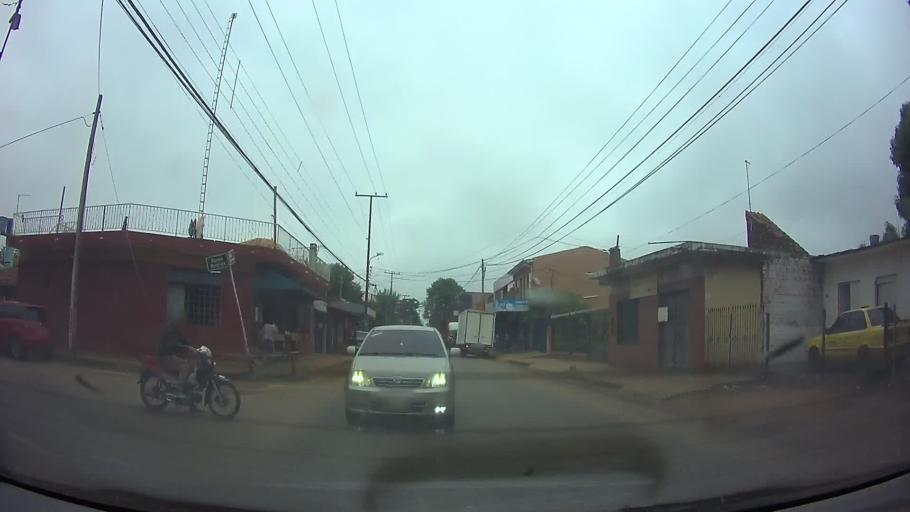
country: PY
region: Central
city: San Lorenzo
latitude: -25.3200
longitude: -57.4964
